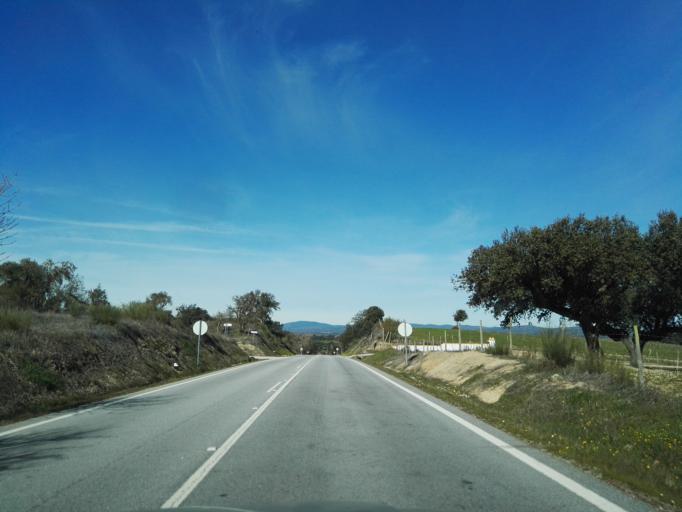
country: PT
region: Portalegre
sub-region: Arronches
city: Arronches
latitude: 39.0840
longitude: -7.2820
